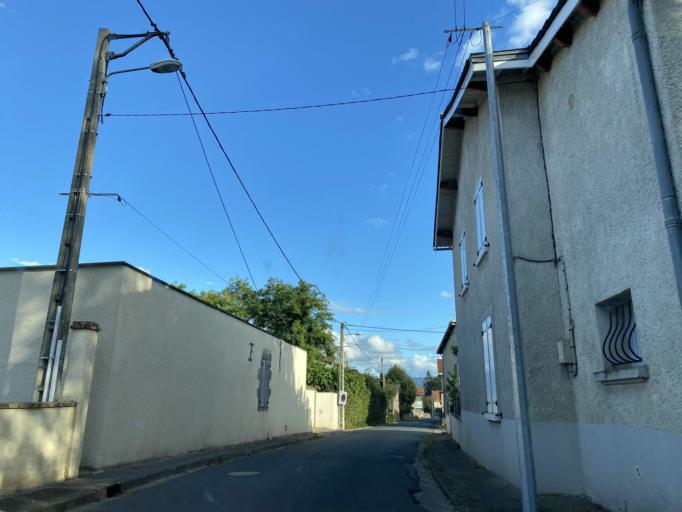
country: FR
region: Auvergne
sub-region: Departement du Puy-de-Dome
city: Puy-Guillaume
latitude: 45.9742
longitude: 3.4432
